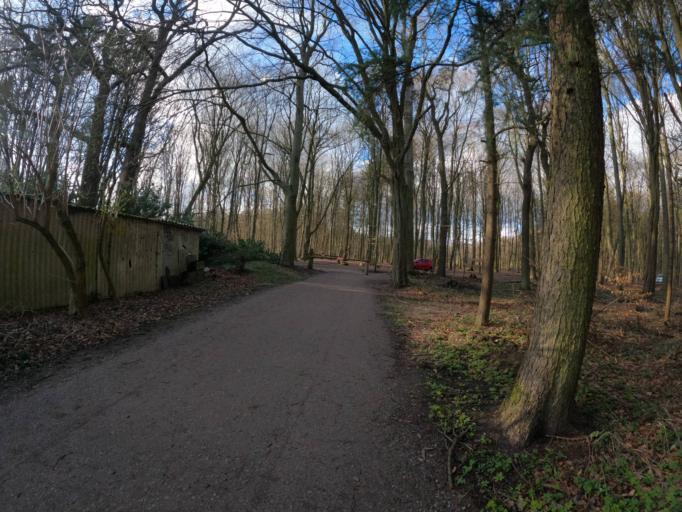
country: DE
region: Hamburg
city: Stellingen
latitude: 53.6129
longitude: 9.9417
